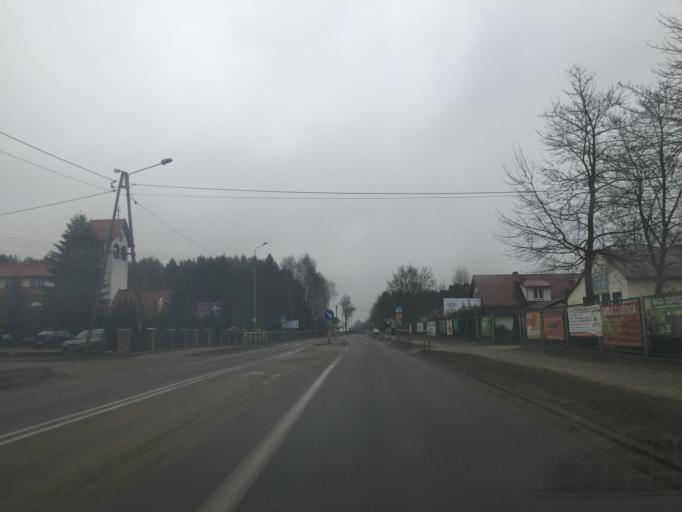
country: PL
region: Pomeranian Voivodeship
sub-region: Powiat kartuski
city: Banino
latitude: 54.3914
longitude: 18.4106
